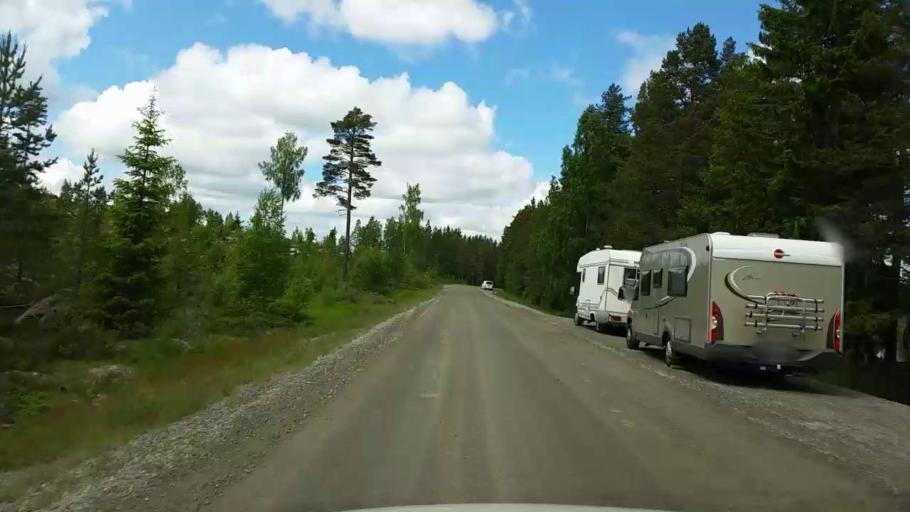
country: SE
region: Gaevleborg
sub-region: Bollnas Kommun
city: Kilafors
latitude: 61.0198
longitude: 16.3799
